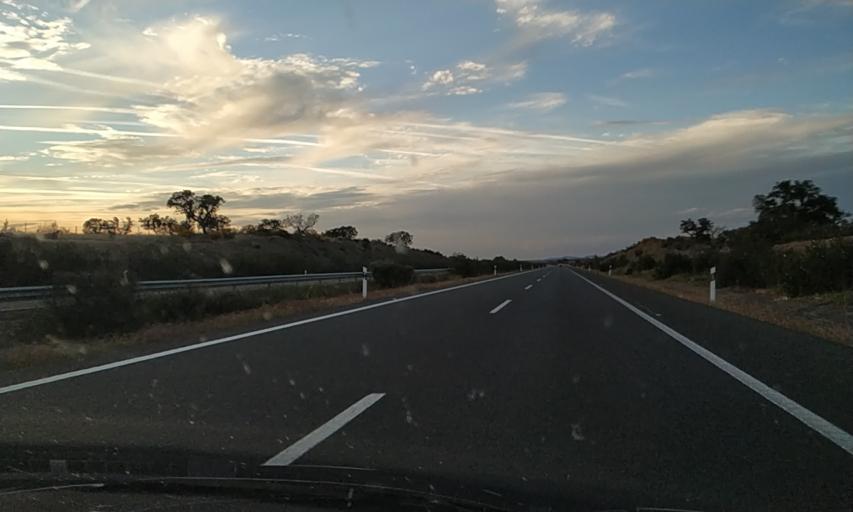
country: ES
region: Extremadura
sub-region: Provincia de Caceres
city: Casas de Don Antonio
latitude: 39.2060
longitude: -6.2836
